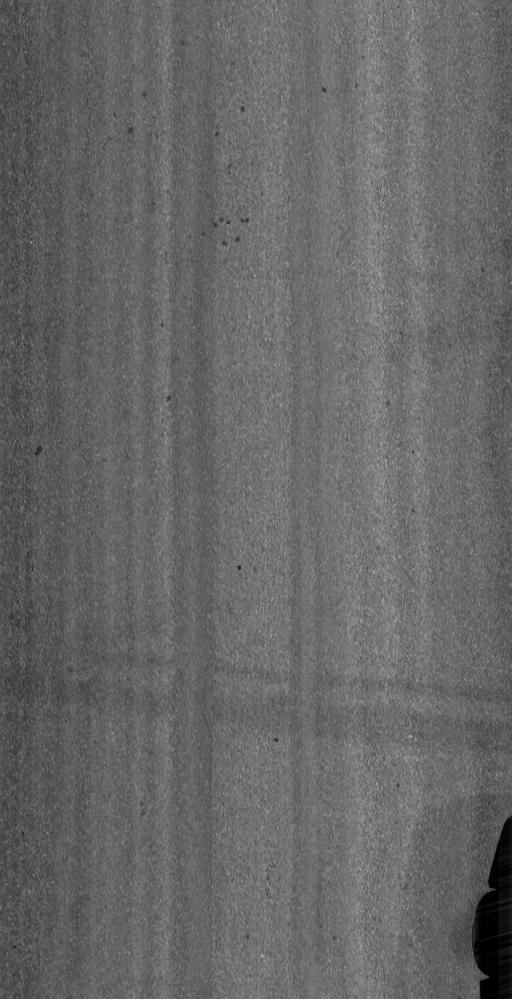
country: US
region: Vermont
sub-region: Chittenden County
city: Burlington
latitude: 44.4896
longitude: -73.2143
